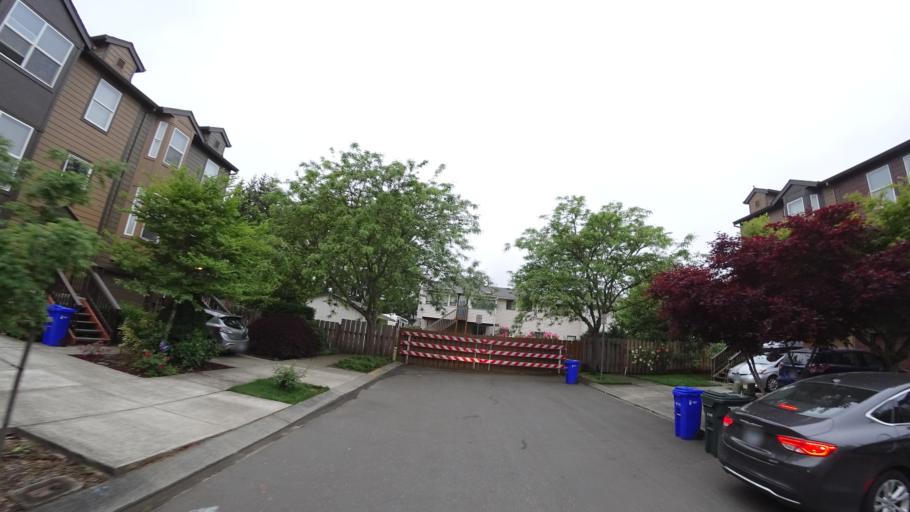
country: US
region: Oregon
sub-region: Washington County
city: Rockcreek
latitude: 45.5227
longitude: -122.9017
